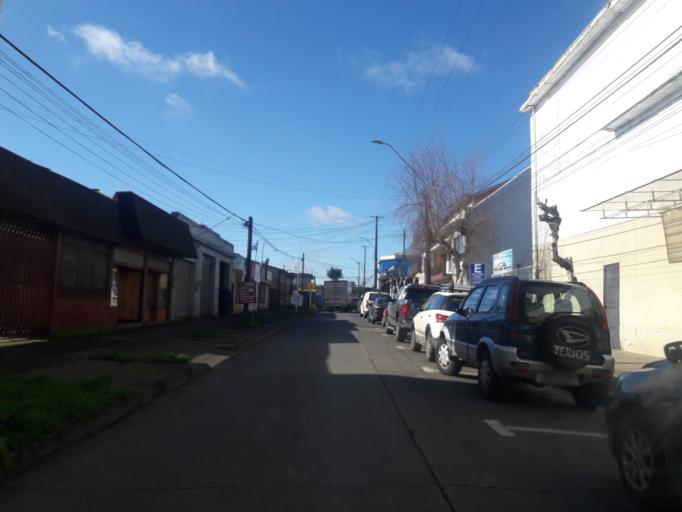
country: CL
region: Araucania
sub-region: Provincia de Malleco
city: Victoria
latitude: -38.2345
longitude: -72.3306
